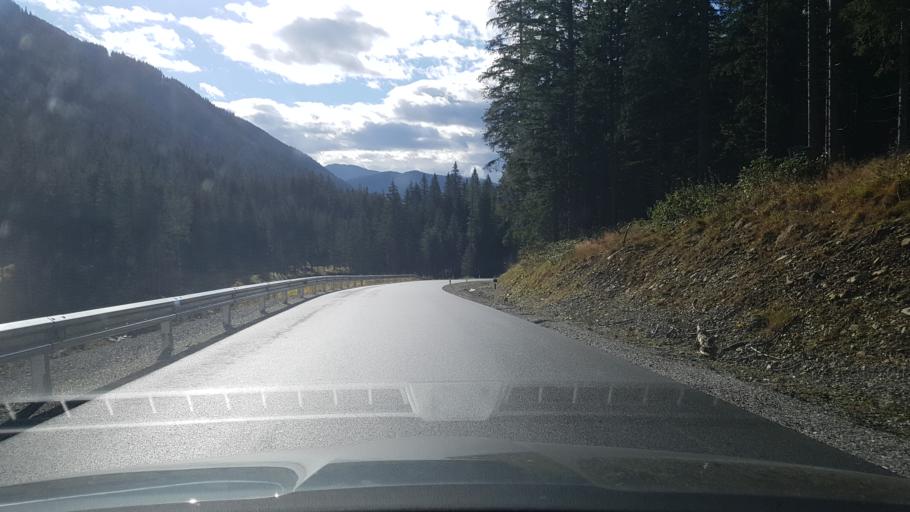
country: AT
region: Styria
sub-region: Politischer Bezirk Murau
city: Schoder
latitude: 47.2284
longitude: 14.0942
